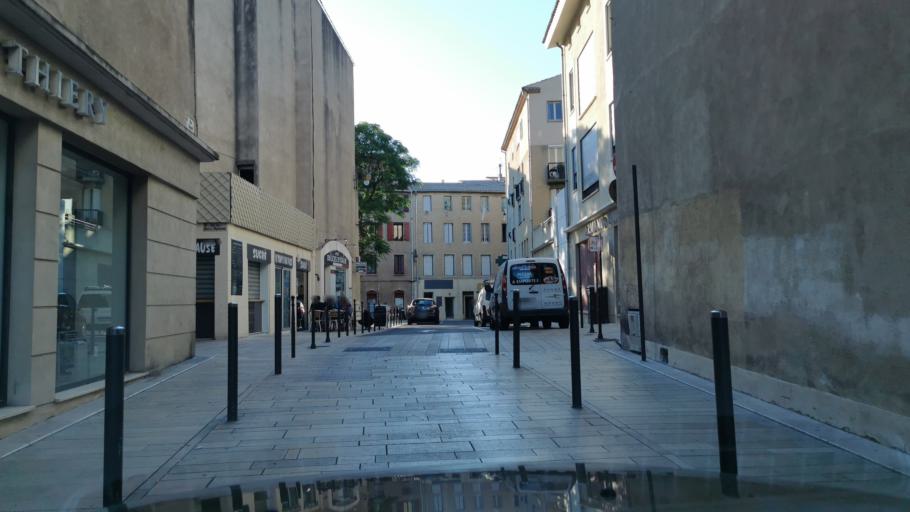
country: FR
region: Languedoc-Roussillon
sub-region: Departement de l'Aude
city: Narbonne
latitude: 43.1828
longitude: 3.0035
